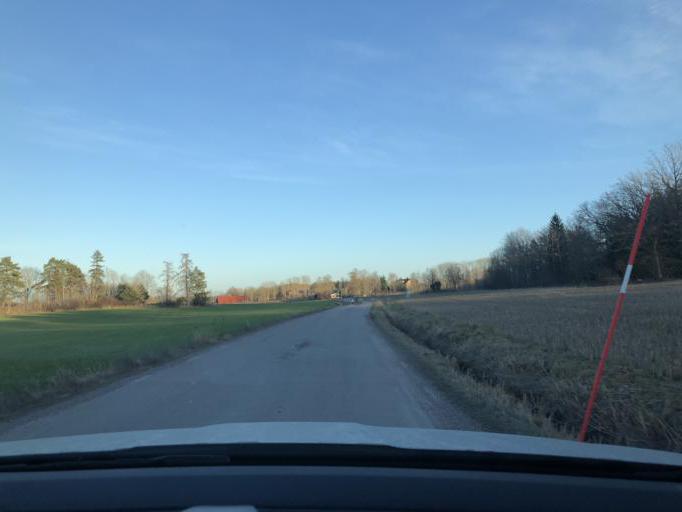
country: SE
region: Soedermanland
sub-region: Eskilstuna Kommun
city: Arla
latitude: 59.4160
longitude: 16.6818
